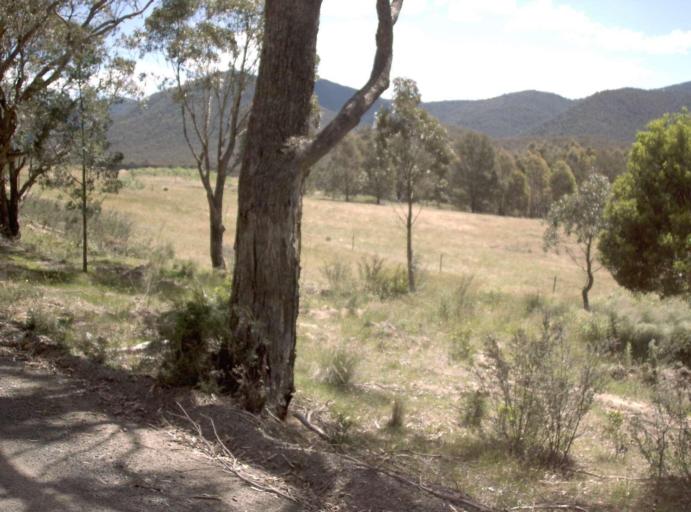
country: AU
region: New South Wales
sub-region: Bombala
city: Bombala
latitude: -37.1464
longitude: 148.6617
